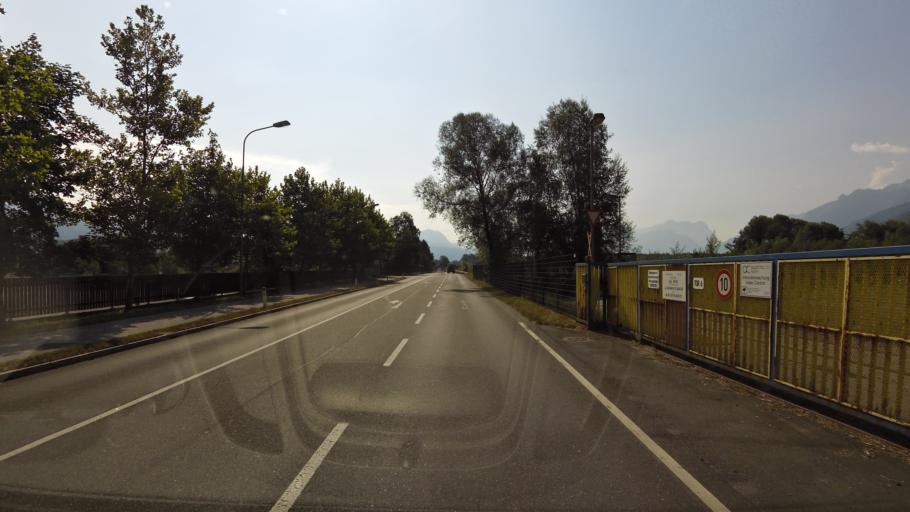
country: AT
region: Salzburg
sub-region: Politischer Bezirk Hallein
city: Hallein
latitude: 47.6735
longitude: 13.1159
